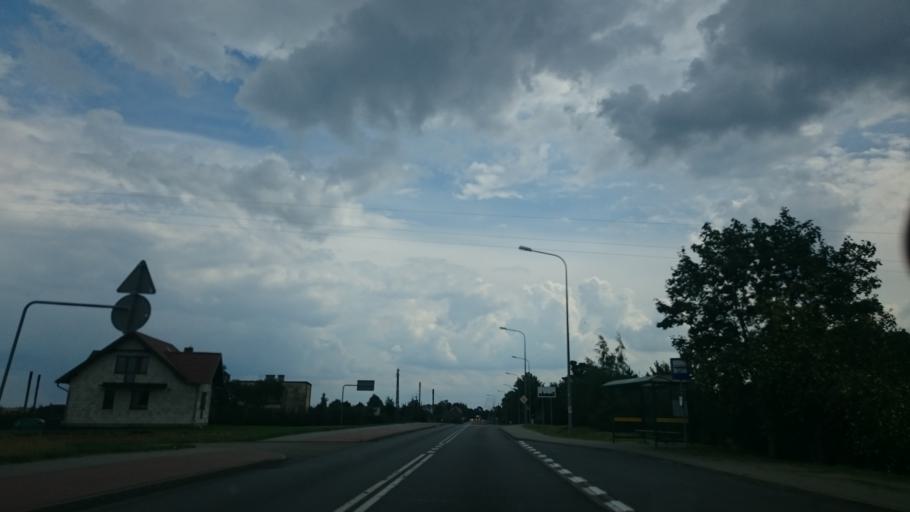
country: PL
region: Kujawsko-Pomorskie
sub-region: Powiat tucholski
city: Kesowo
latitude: 53.6547
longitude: 17.6921
